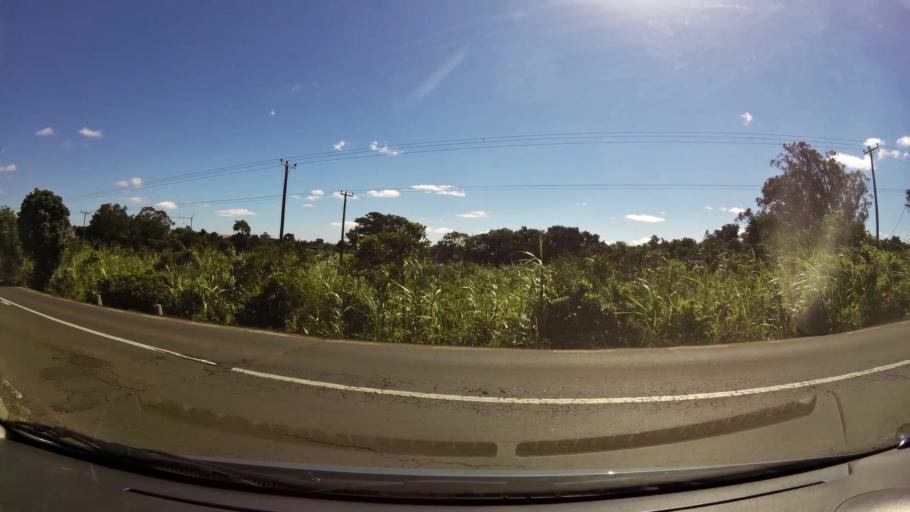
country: MU
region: Plaines Wilhems
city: Curepipe
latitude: -20.3405
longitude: 57.4939
